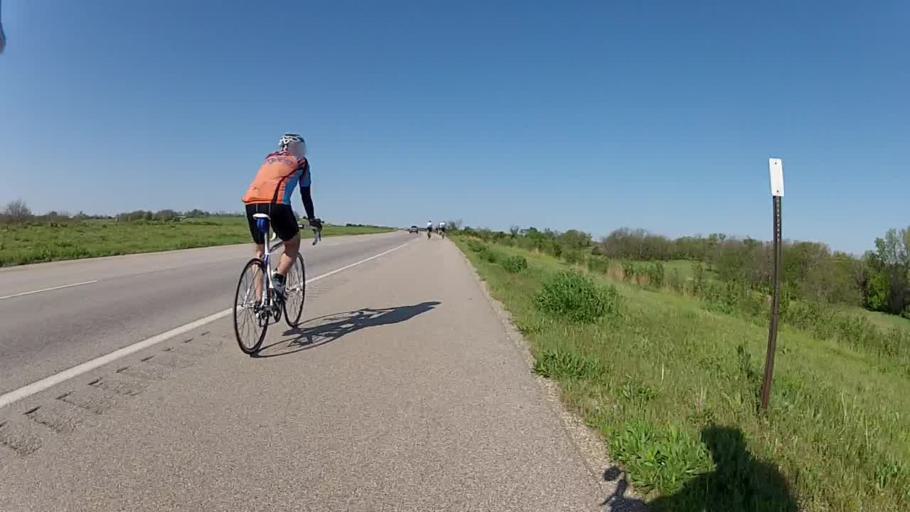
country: US
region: Kansas
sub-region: Riley County
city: Ogden
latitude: 39.0824
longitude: -96.7282
